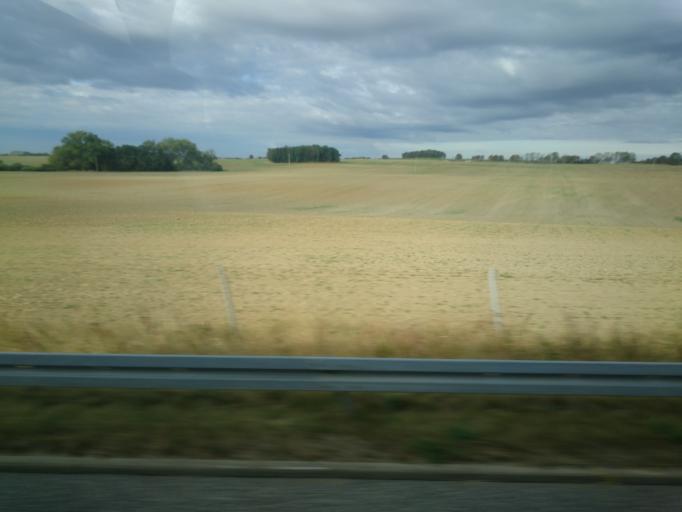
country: DE
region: Brandenburg
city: Schonfeld
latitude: 53.4046
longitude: 13.9956
